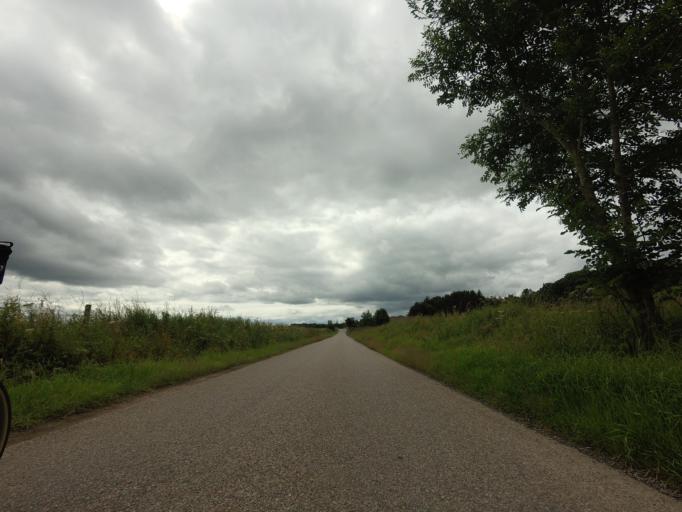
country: GB
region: Scotland
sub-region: Moray
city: Forres
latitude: 57.6014
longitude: -3.6946
